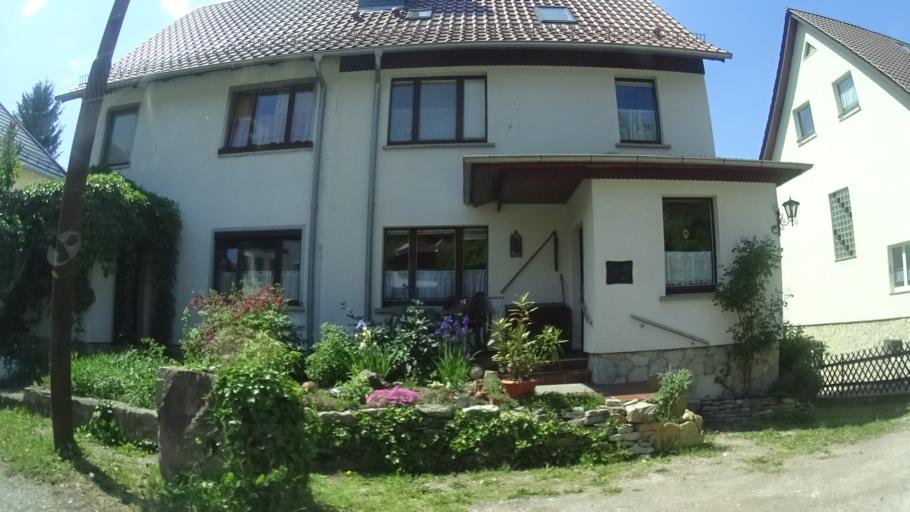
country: DE
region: Thuringia
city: Arnstadt
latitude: 50.8307
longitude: 10.9372
